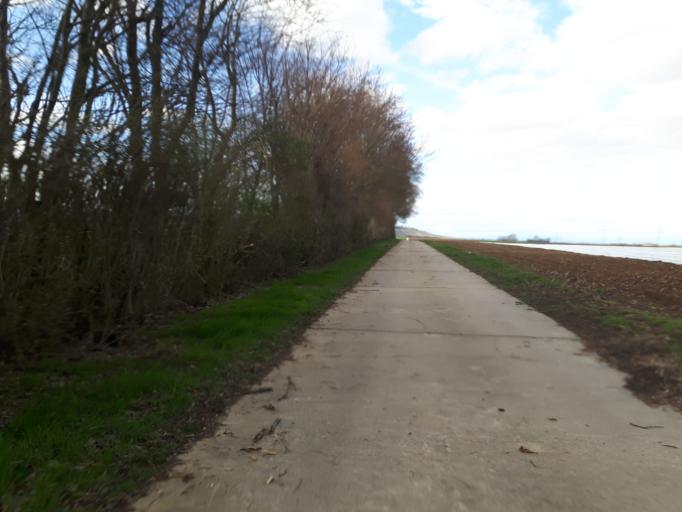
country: DE
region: Baden-Wuerttemberg
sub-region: Regierungsbezirk Stuttgart
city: Nordheim
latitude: 49.0873
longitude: 9.1162
